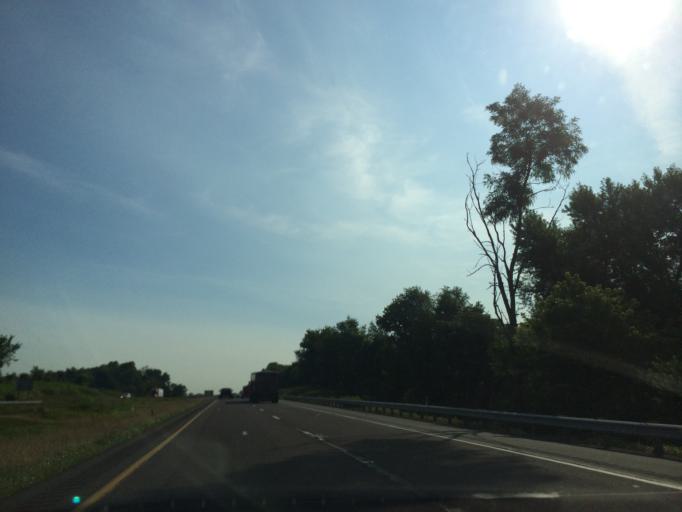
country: US
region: Pennsylvania
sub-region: Lancaster County
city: Lancaster
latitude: 40.0780
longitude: -76.2820
